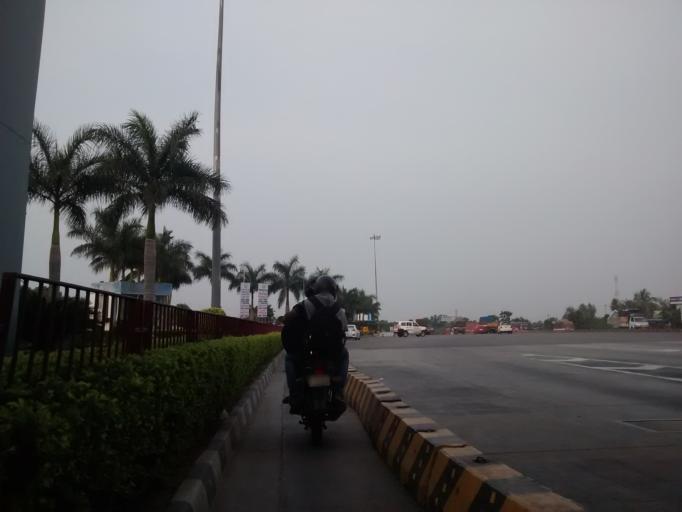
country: IN
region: Tamil Nadu
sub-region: Dharmapuri
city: Dharmapuri
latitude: 12.0066
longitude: 78.0804
